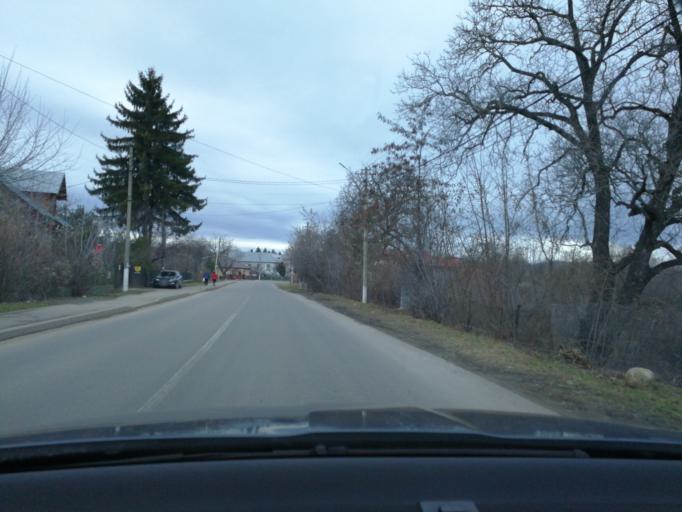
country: RO
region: Prahova
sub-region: Oras Breaza
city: Breaza de Jos
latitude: 45.1699
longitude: 25.6766
